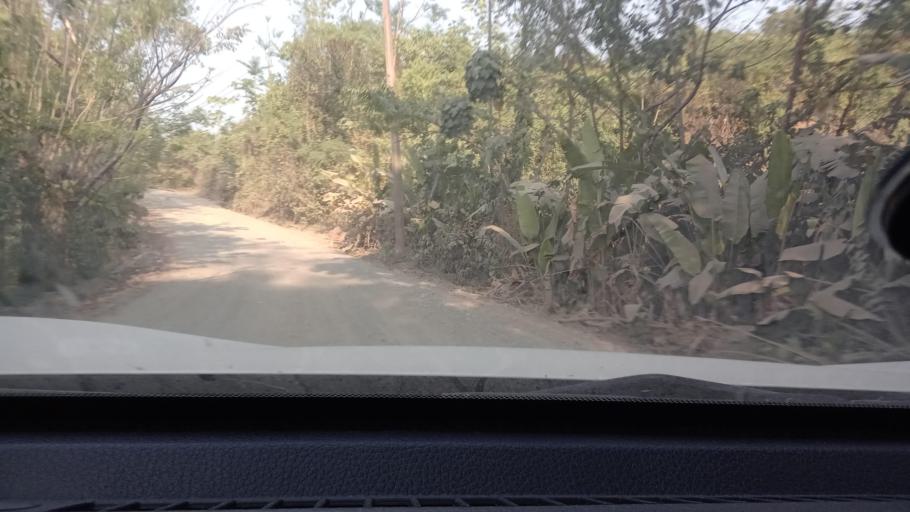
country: MX
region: Tabasco
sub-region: Huimanguillo
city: Francisco Rueda
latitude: 17.6563
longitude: -93.8692
